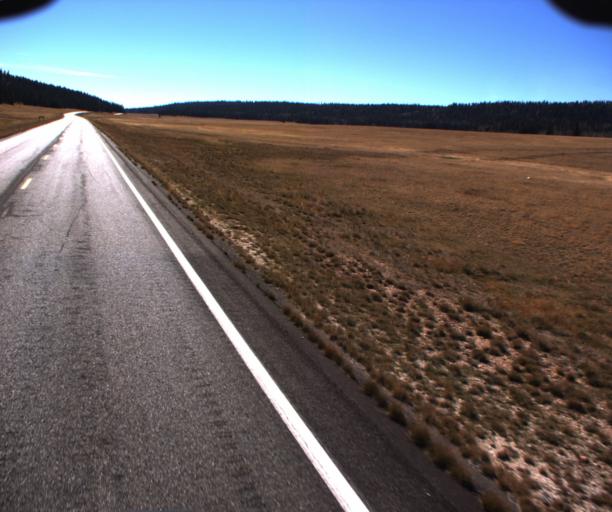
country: US
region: Arizona
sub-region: Coconino County
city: Grand Canyon
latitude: 36.3945
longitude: -112.1280
